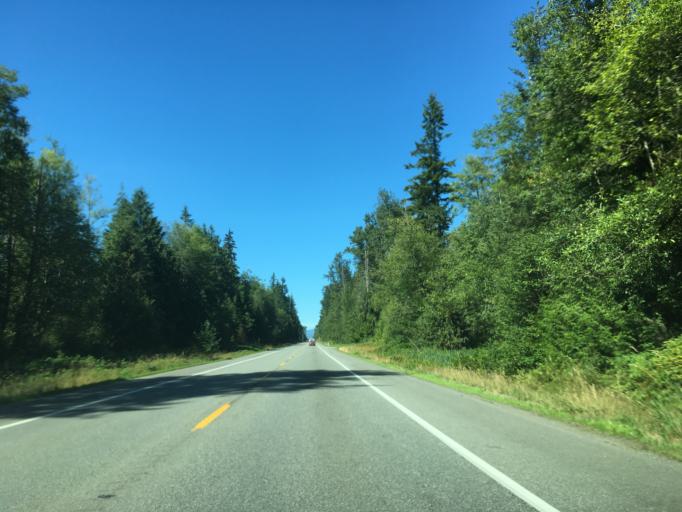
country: US
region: Washington
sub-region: Snohomish County
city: Sisco Heights
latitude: 48.1077
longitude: -122.1122
